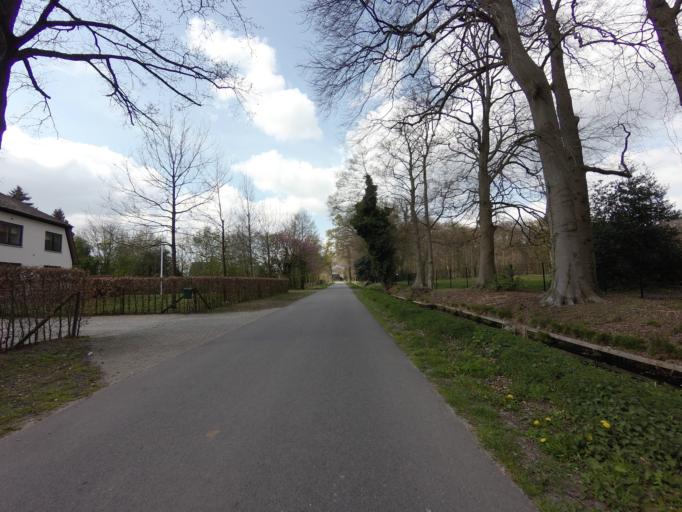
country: NL
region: Utrecht
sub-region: Gemeente Utrechtse Heuvelrug
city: Doorn
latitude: 52.0282
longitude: 5.3379
